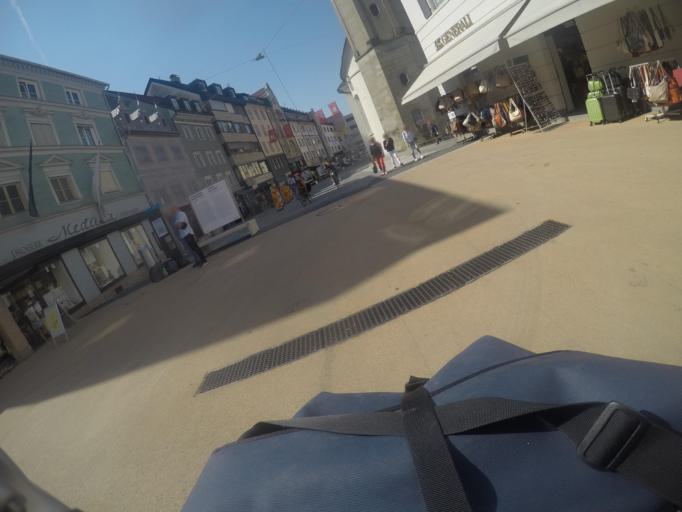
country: AT
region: Vorarlberg
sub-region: Politischer Bezirk Bregenz
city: Bregenz
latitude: 47.5030
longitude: 9.7472
